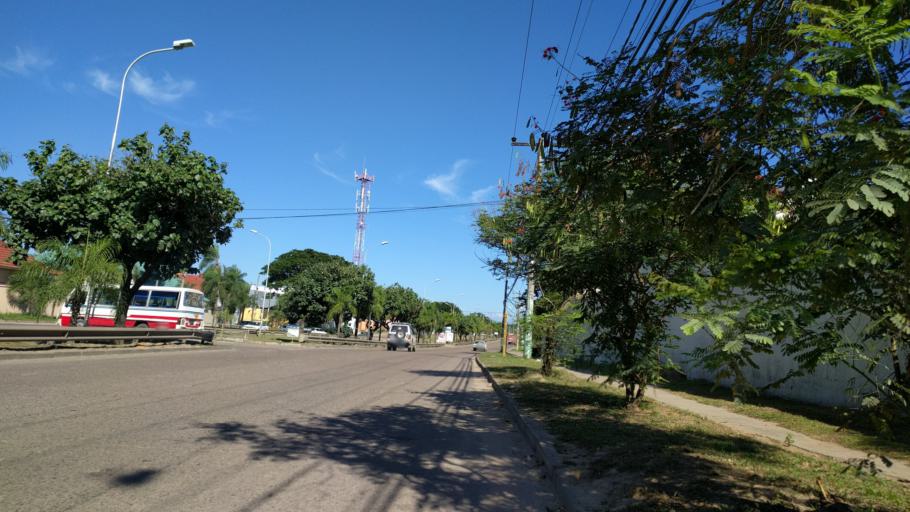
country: BO
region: Santa Cruz
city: Santa Cruz de la Sierra
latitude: -17.7988
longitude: -63.2191
